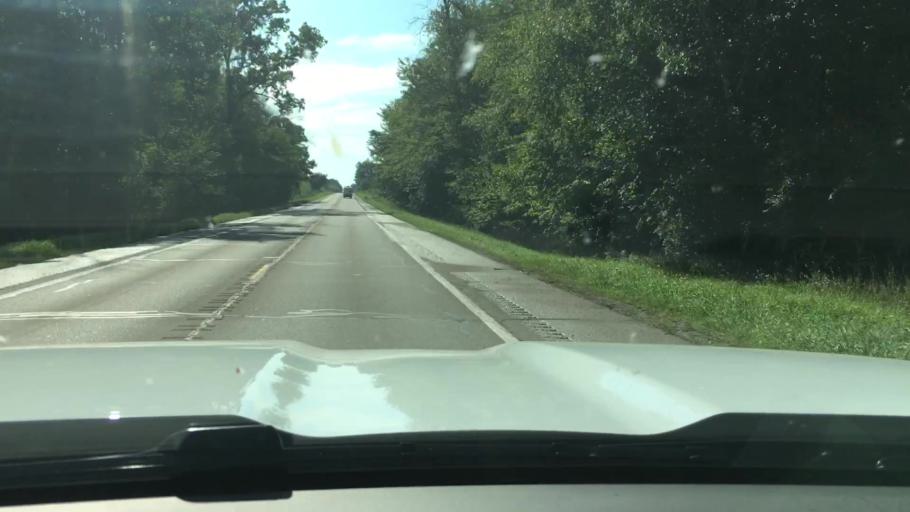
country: US
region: Michigan
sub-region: Montcalm County
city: Edmore
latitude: 43.4240
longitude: -85.1434
